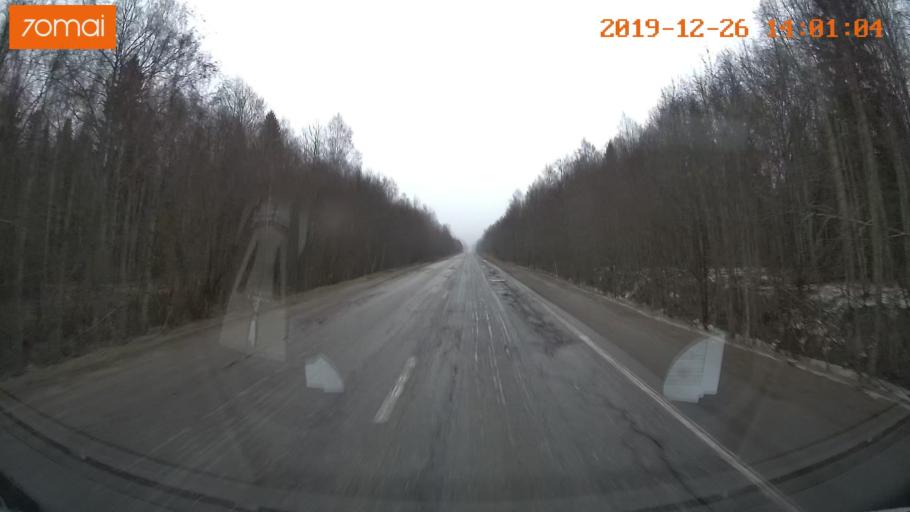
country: RU
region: Jaroslavl
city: Poshekhon'ye
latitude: 58.5533
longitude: 38.7563
